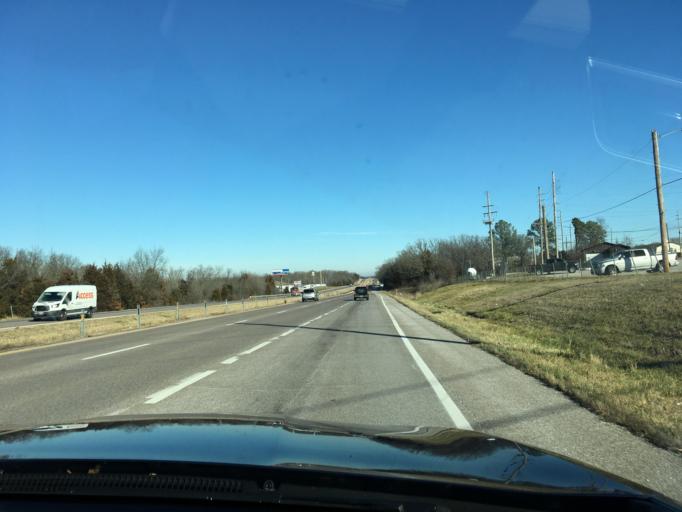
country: US
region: Missouri
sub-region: Jefferson County
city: De Soto
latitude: 38.1395
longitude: -90.4699
